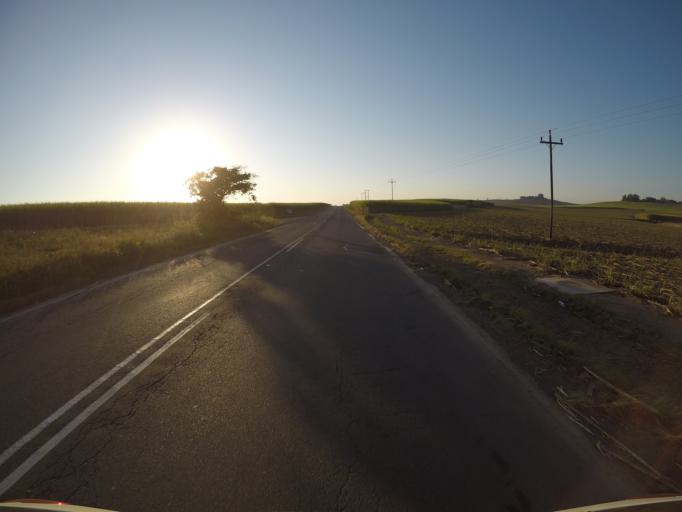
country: ZA
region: KwaZulu-Natal
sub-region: uThungulu District Municipality
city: eSikhawini
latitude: -28.9485
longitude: 31.7231
